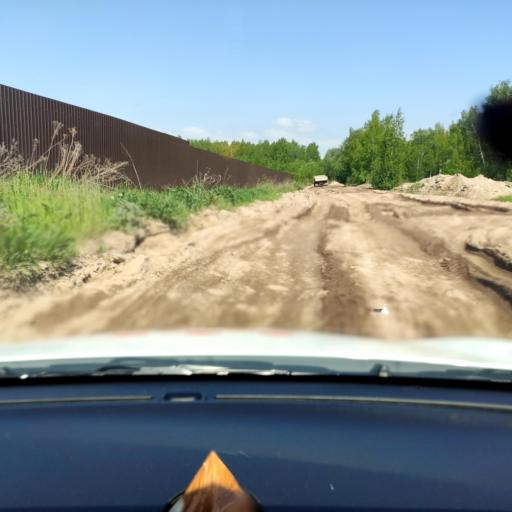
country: RU
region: Tatarstan
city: Stolbishchi
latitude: 55.7045
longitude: 49.1812
